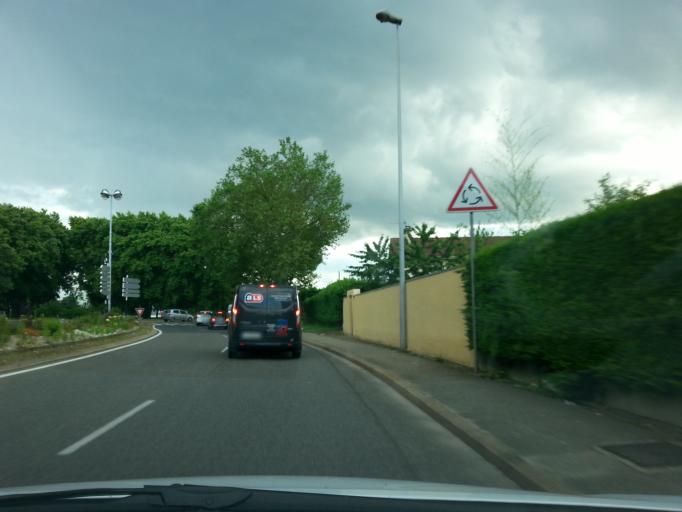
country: FR
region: Rhone-Alpes
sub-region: Departement du Rhone
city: Rillieux-la-Pape
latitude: 45.8178
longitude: 4.8918
